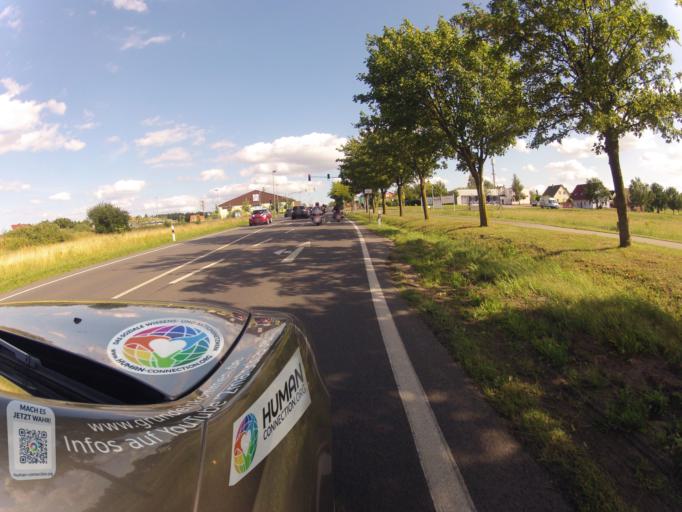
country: DE
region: Mecklenburg-Vorpommern
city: Loddin
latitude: 54.0157
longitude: 14.0459
